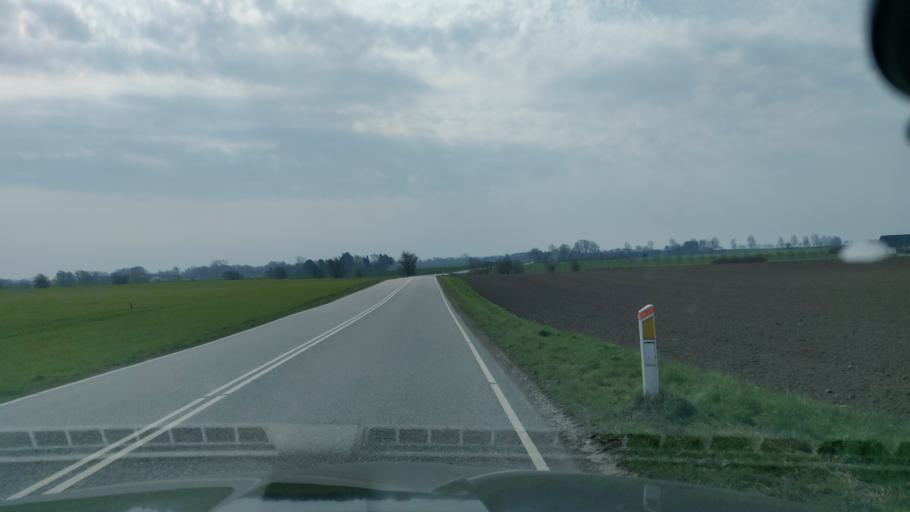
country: DK
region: South Denmark
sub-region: Nordfyns Kommune
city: Sonderso
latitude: 55.5058
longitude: 10.2501
